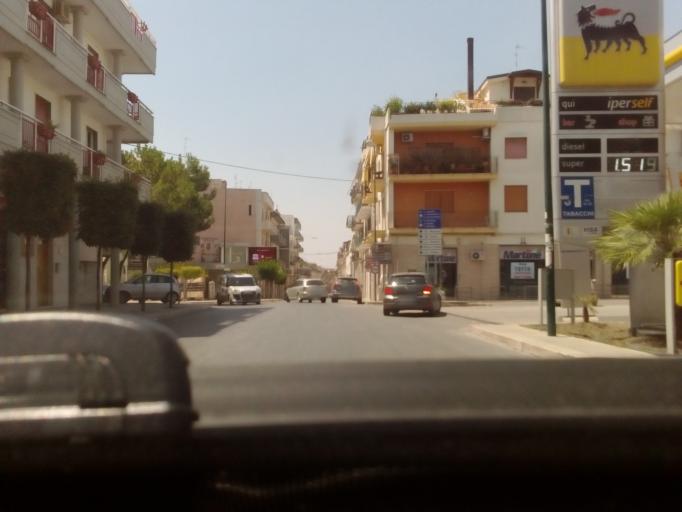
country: IT
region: Apulia
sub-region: Provincia di Bari
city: Gravina in Puglia
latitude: 40.8177
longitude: 16.4259
